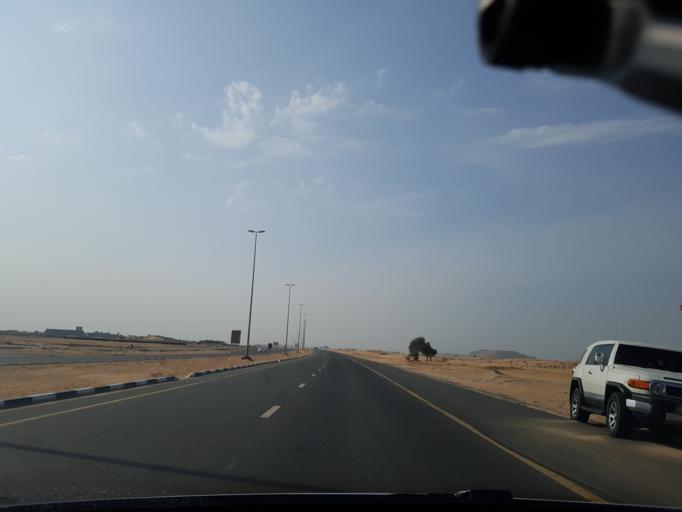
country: AE
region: Ajman
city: Ajman
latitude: 25.4082
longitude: 55.5731
